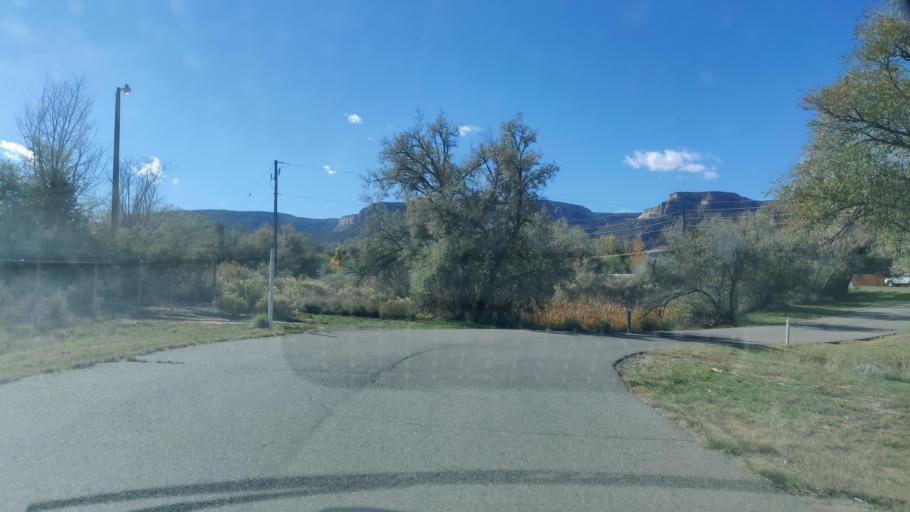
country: US
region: Colorado
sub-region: Mesa County
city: Redlands
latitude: 39.0694
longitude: -108.6438
